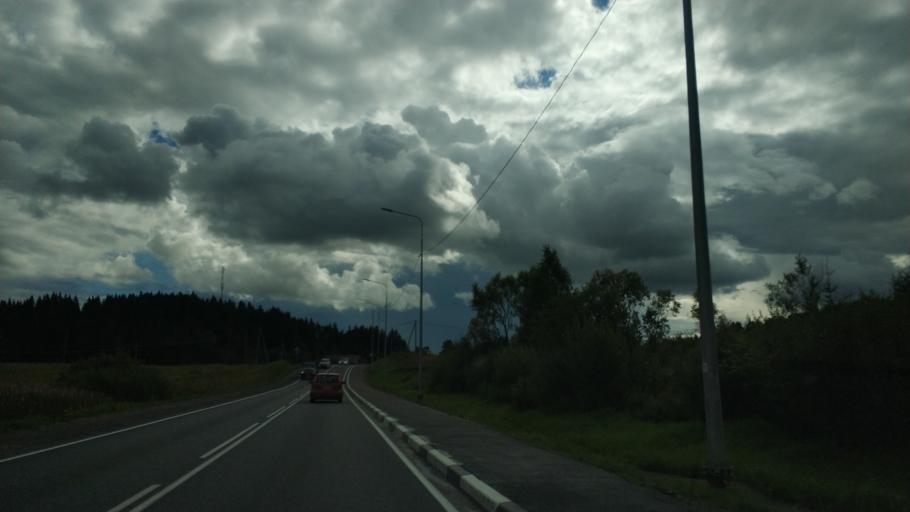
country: RU
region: Republic of Karelia
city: Khelyulya
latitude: 61.7605
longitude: 30.6570
